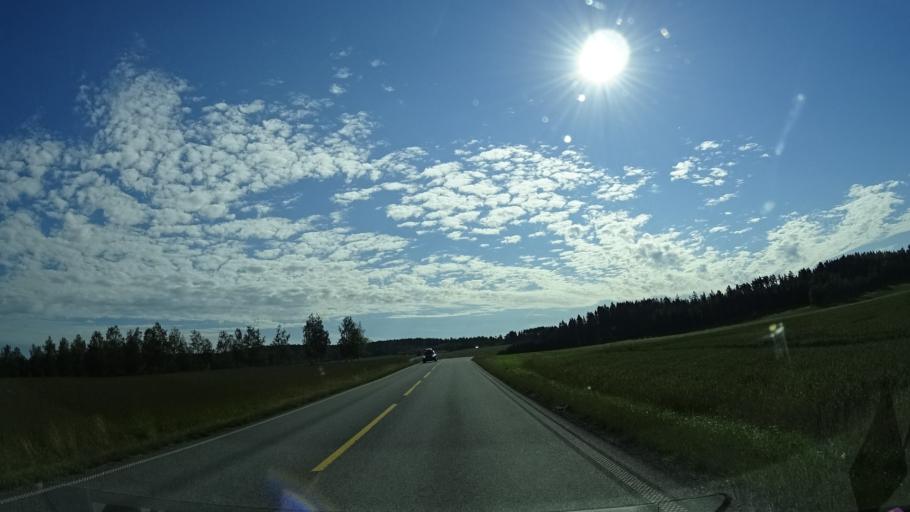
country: NO
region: Ostfold
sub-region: Eidsberg
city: Mysen
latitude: 59.5537
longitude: 11.3852
